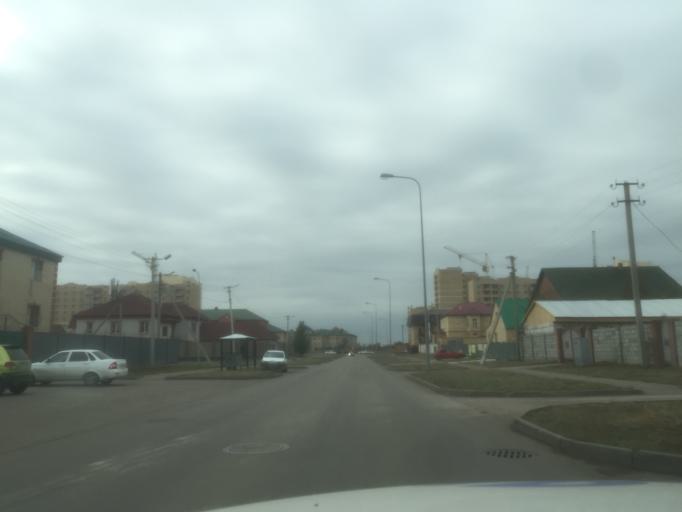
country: KZ
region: Astana Qalasy
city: Astana
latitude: 51.1751
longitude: 71.3726
